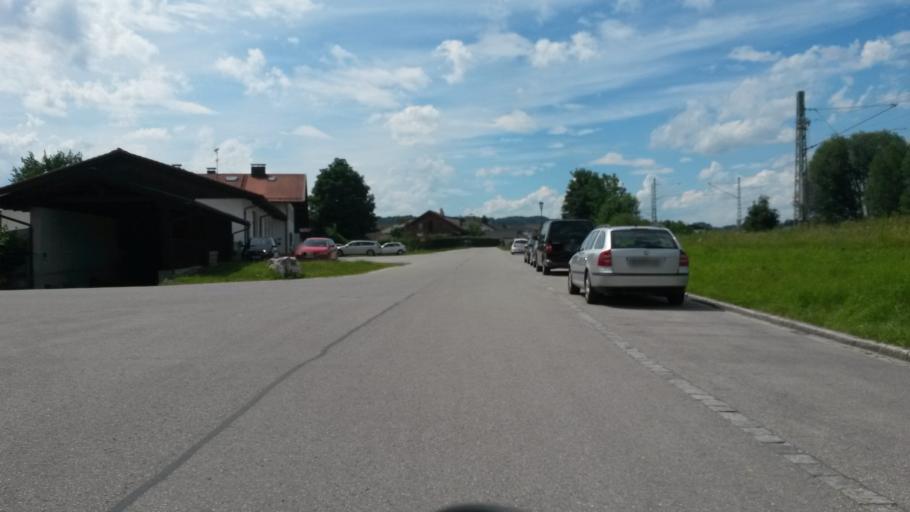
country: DE
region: Bavaria
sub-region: Upper Bavaria
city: Bernau am Chiemsee
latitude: 47.8141
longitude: 12.3873
